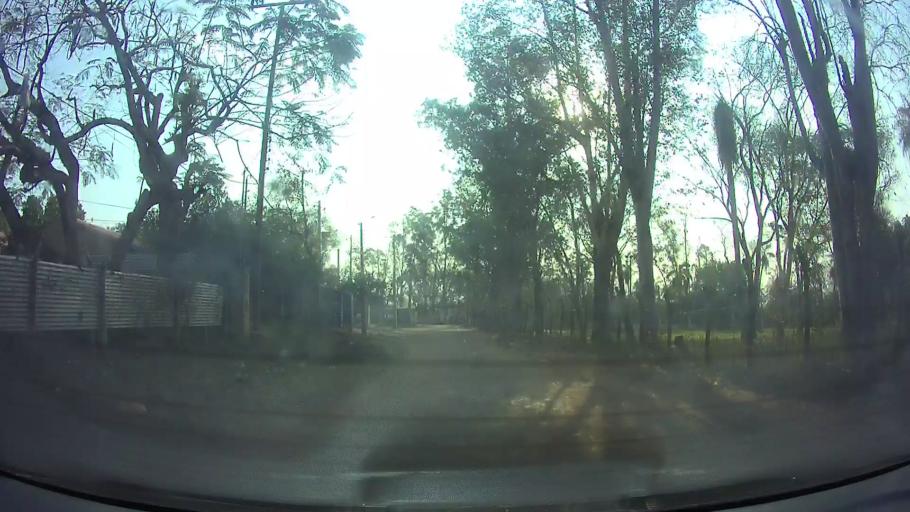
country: PY
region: Central
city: Limpio
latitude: -25.2193
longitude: -57.5016
